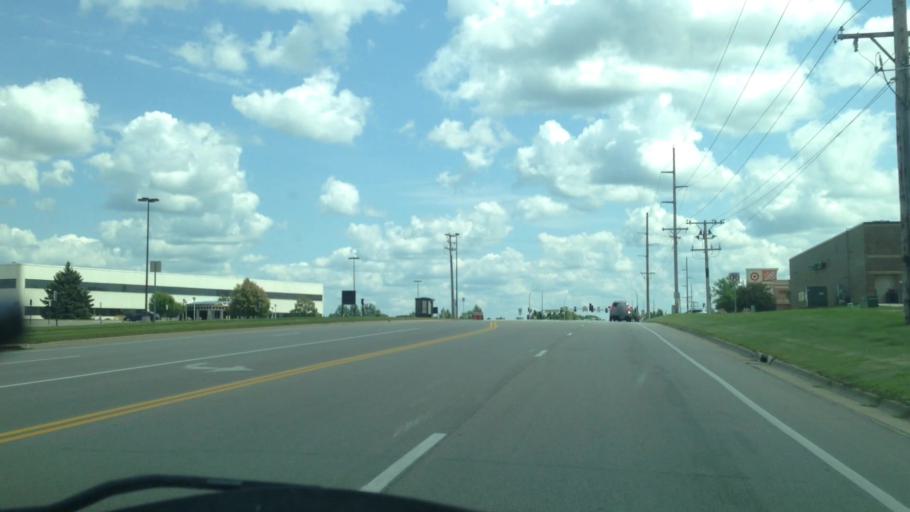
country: US
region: Minnesota
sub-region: Olmsted County
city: Rochester
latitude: 44.0653
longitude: -92.5068
